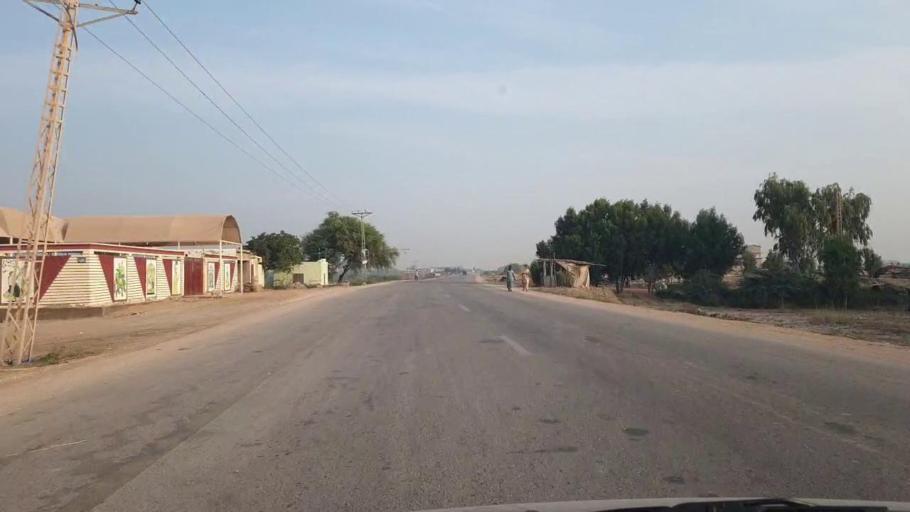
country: PK
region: Sindh
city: Badin
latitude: 24.6880
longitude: 68.8237
